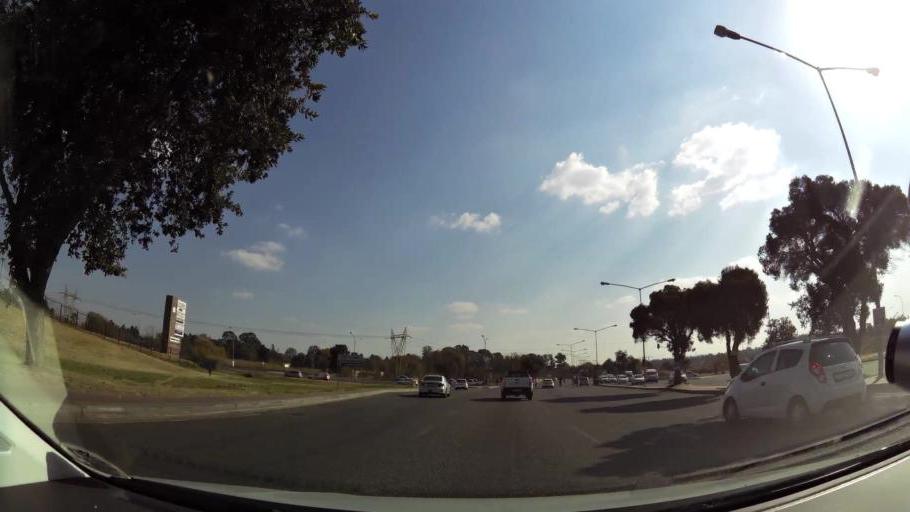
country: ZA
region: Gauteng
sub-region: City of Johannesburg Metropolitan Municipality
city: Modderfontein
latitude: -26.1011
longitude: 28.2214
